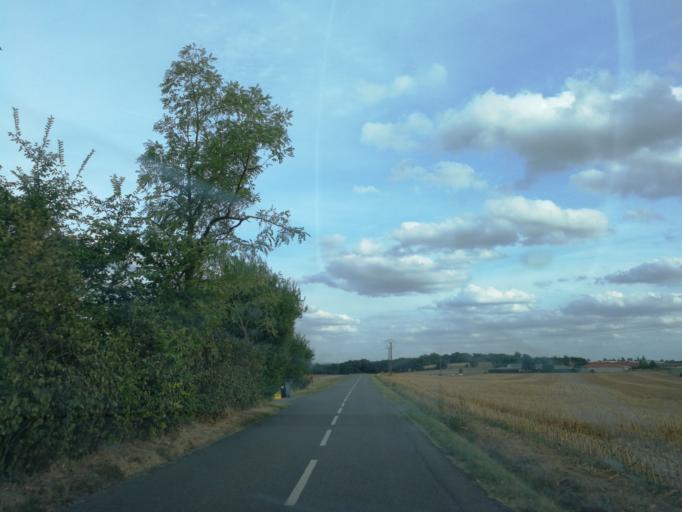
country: FR
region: Midi-Pyrenees
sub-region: Departement de la Haute-Garonne
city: Flourens
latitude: 43.6083
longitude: 1.5389
